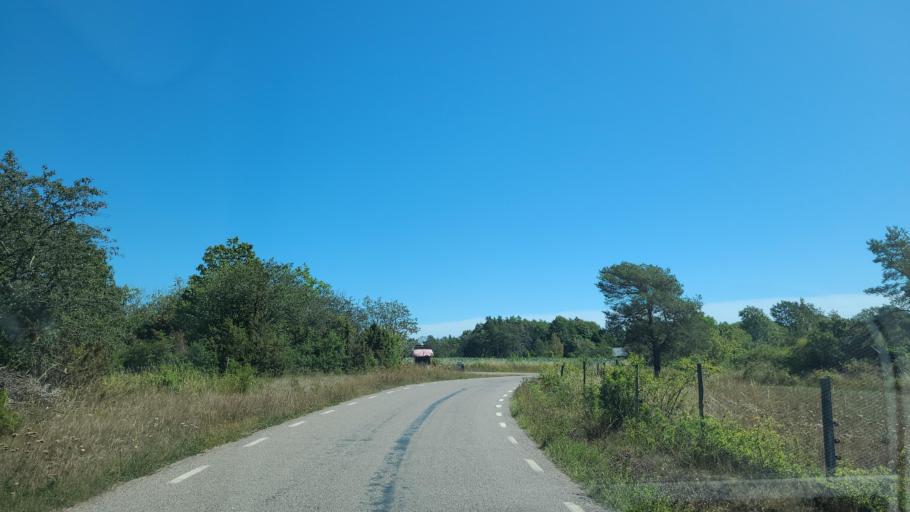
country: SE
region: Kalmar
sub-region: Borgholms Kommun
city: Borgholm
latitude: 56.7469
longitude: 16.6865
